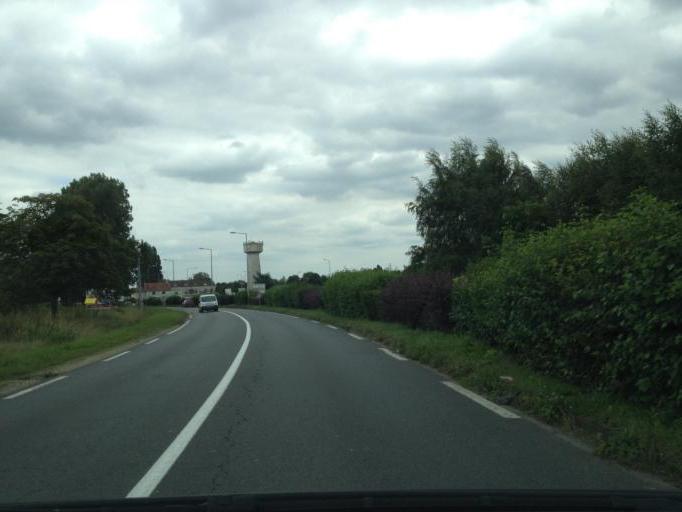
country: FR
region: Ile-de-France
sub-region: Departement de l'Essonne
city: Saclay
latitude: 48.7302
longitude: 2.1601
